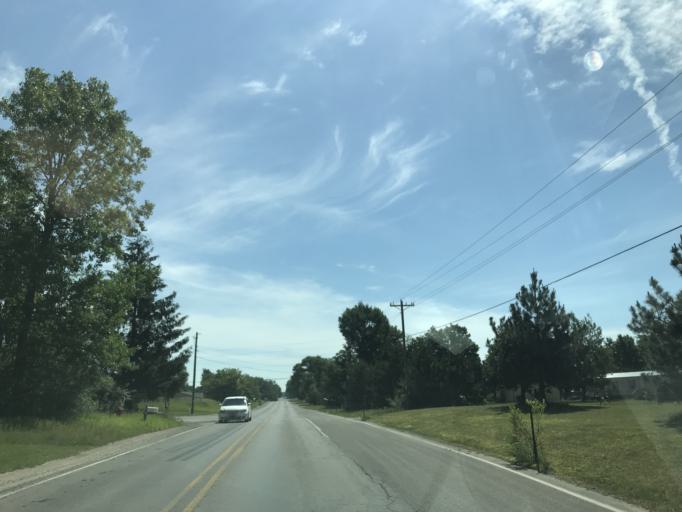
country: US
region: Michigan
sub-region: Grand Traverse County
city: Traverse City
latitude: 44.6576
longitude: -85.6682
